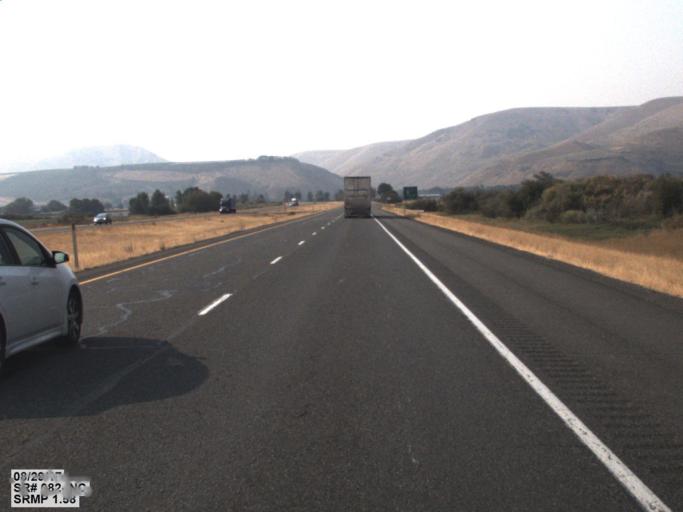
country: US
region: Washington
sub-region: Kittitas County
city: Ellensburg
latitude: 46.9488
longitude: -120.5079
